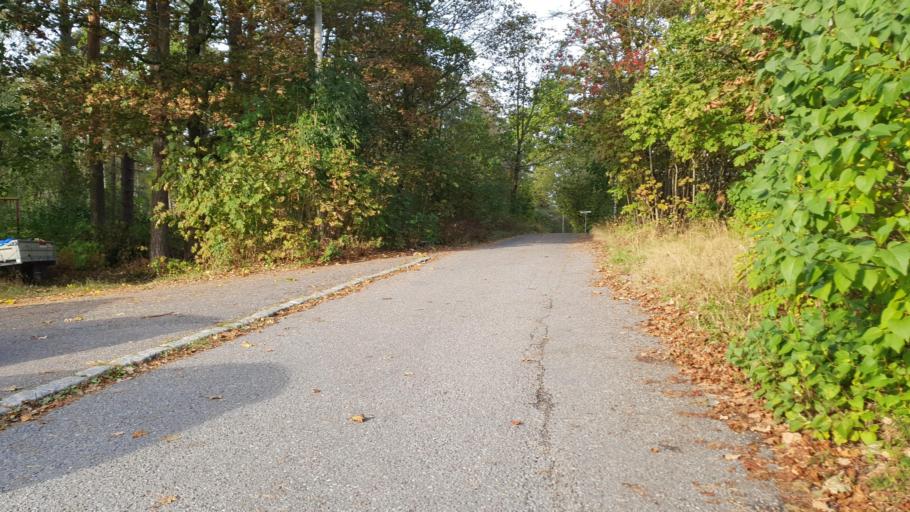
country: NO
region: Vestfold
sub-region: Tonsberg
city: Tonsberg
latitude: 59.2809
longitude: 10.4261
